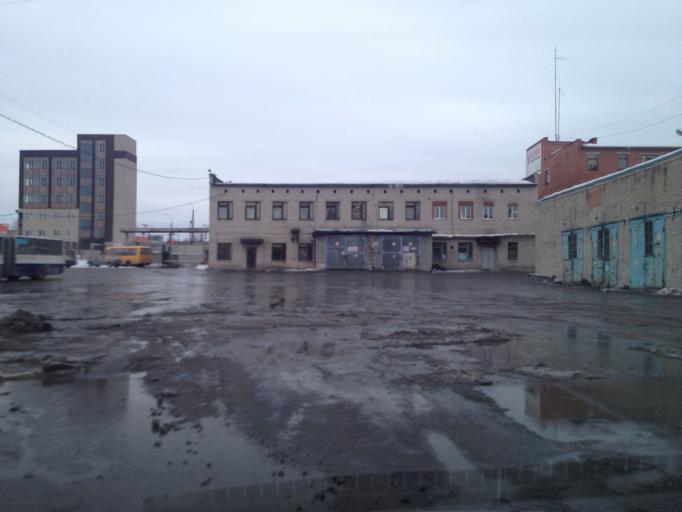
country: RU
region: Sverdlovsk
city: Sovkhoznyy
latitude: 56.8108
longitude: 60.5412
